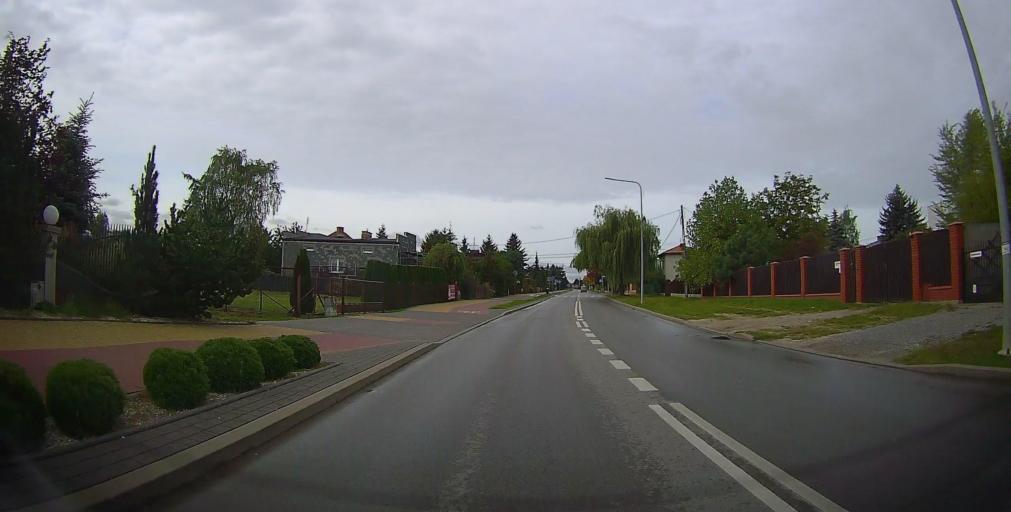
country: PL
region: Masovian Voivodeship
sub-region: Powiat grojecki
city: Grojec
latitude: 51.8602
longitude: 20.8739
